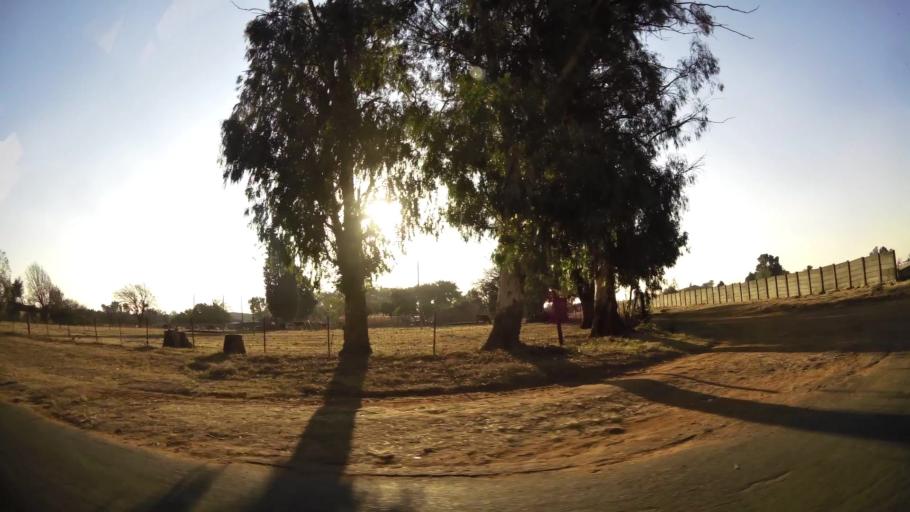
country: ZA
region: Gauteng
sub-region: West Rand District Municipality
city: Randfontein
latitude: -26.2158
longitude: 27.6541
